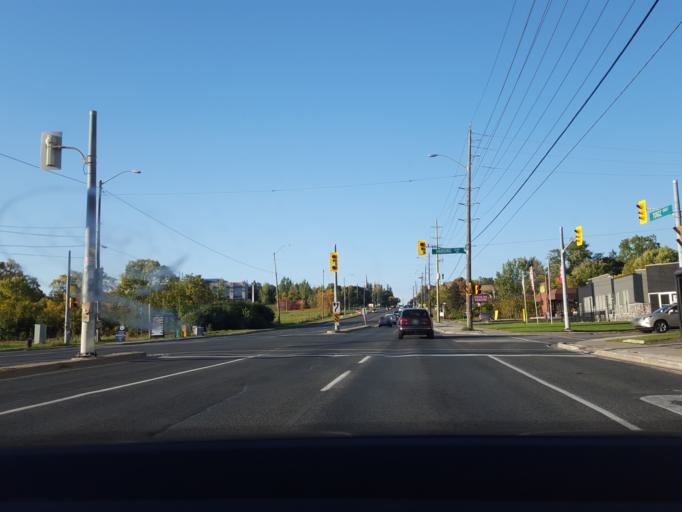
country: CA
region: Ontario
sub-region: York
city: Richmond Hill
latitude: 43.8663
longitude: -79.4360
